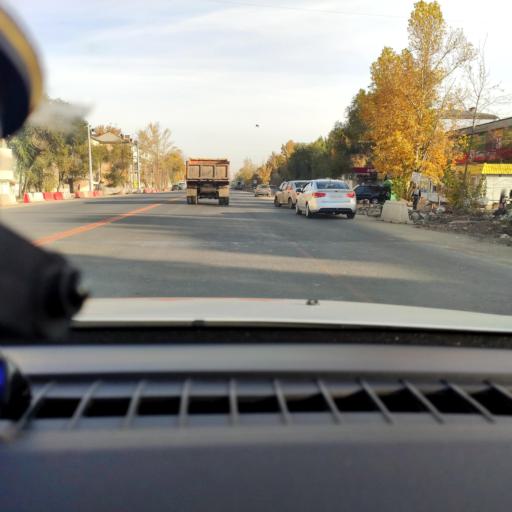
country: RU
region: Samara
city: Samara
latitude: 53.1211
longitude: 50.0873
